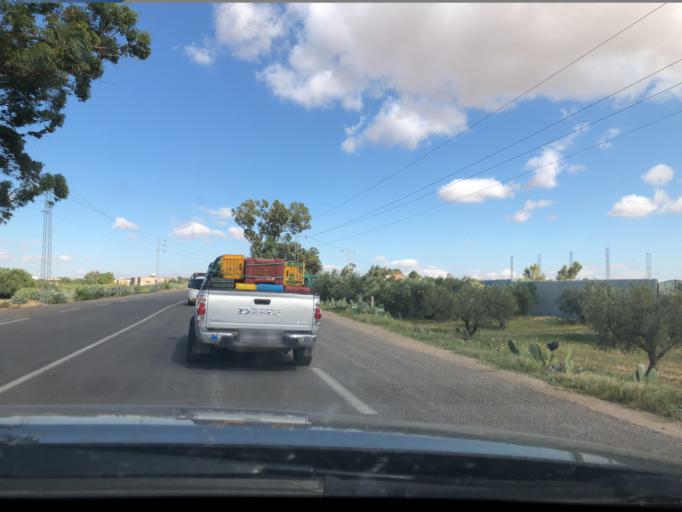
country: TN
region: Al Qasrayn
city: Kasserine
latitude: 35.2039
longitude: 8.8800
